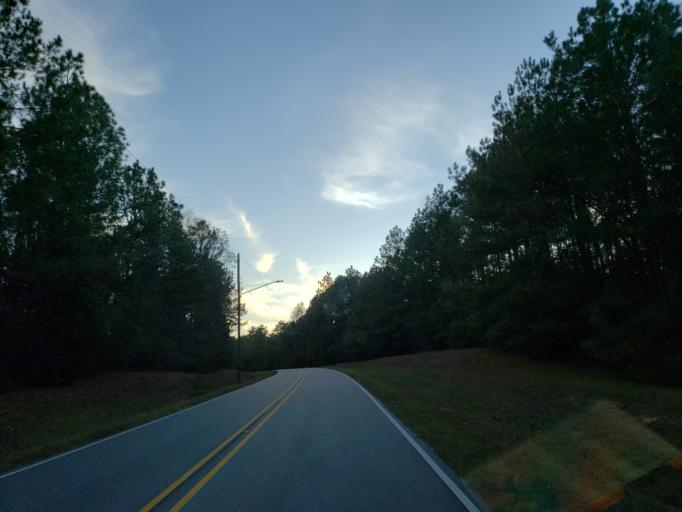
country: US
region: Mississippi
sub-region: Forrest County
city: Hattiesburg
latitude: 31.2633
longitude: -89.3120
